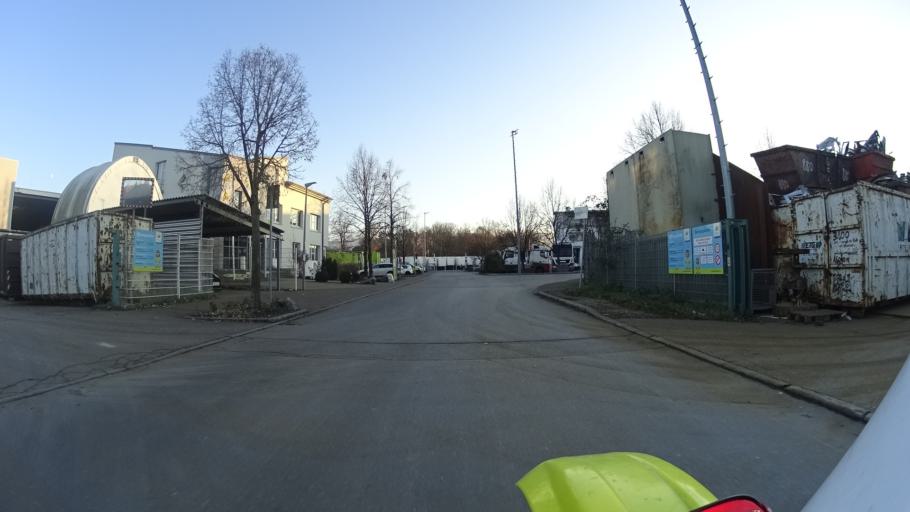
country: DE
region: Baden-Wuerttemberg
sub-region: Regierungsbezirk Stuttgart
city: Eislingen
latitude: 48.6798
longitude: 9.6896
